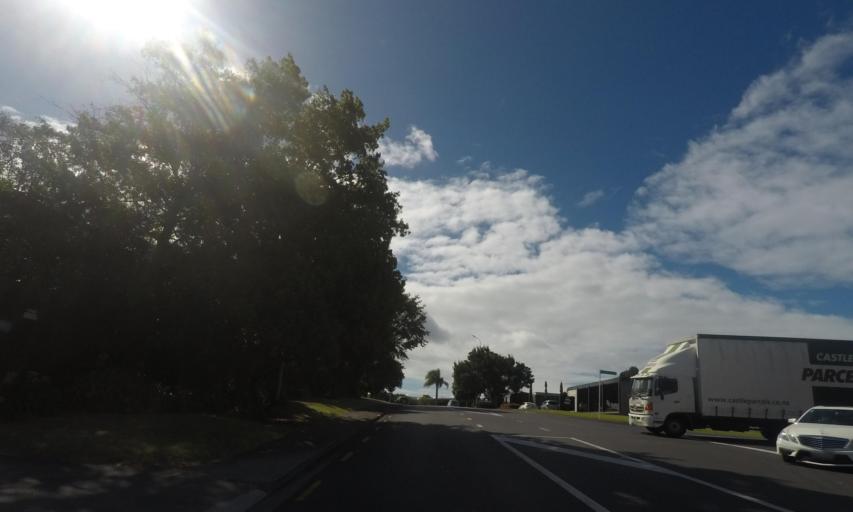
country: NZ
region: Auckland
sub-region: Auckland
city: Tamaki
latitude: -36.9243
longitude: 174.8520
